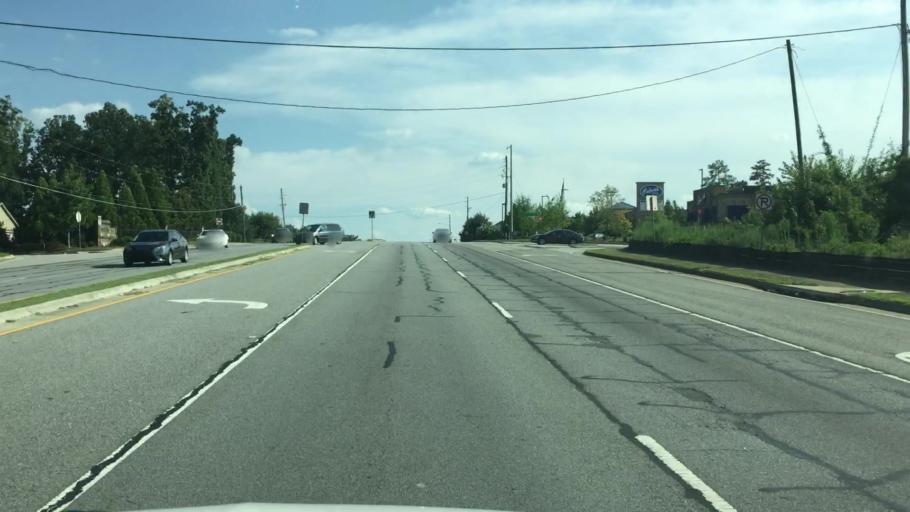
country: US
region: Georgia
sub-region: Gwinnett County
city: Grayson
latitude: 33.9074
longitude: -84.0033
